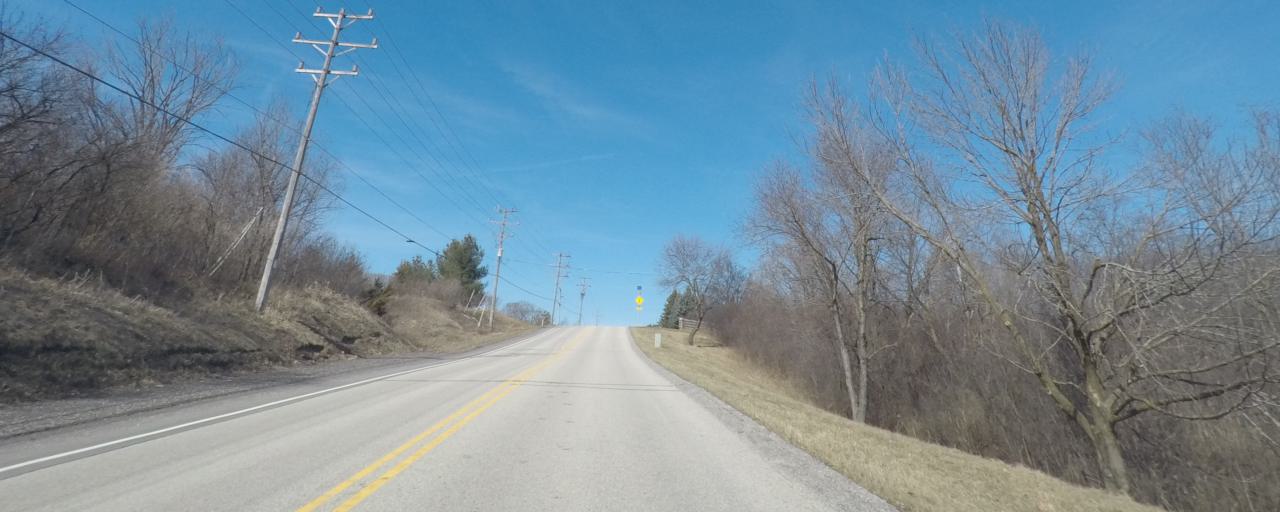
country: US
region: Wisconsin
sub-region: Waukesha County
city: Merton
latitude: 43.1512
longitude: -88.3266
